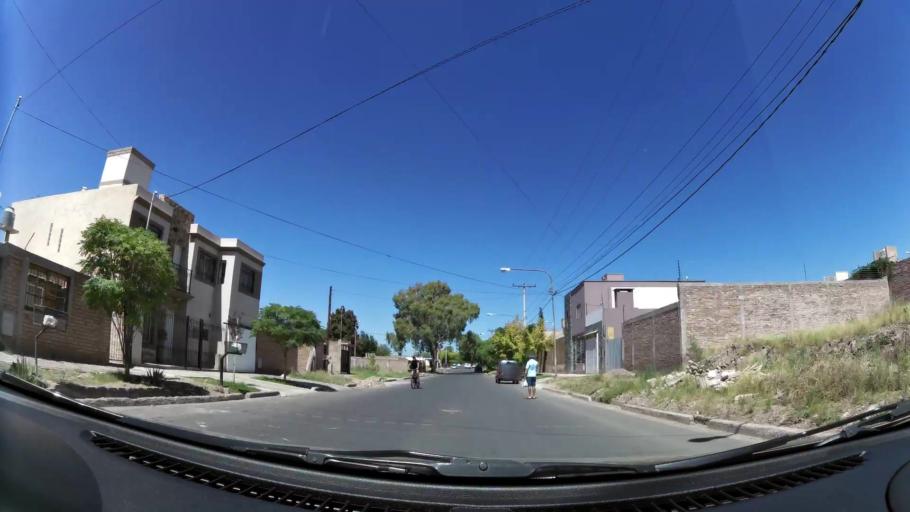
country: AR
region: Mendoza
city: Las Heras
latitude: -32.8406
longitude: -68.8719
